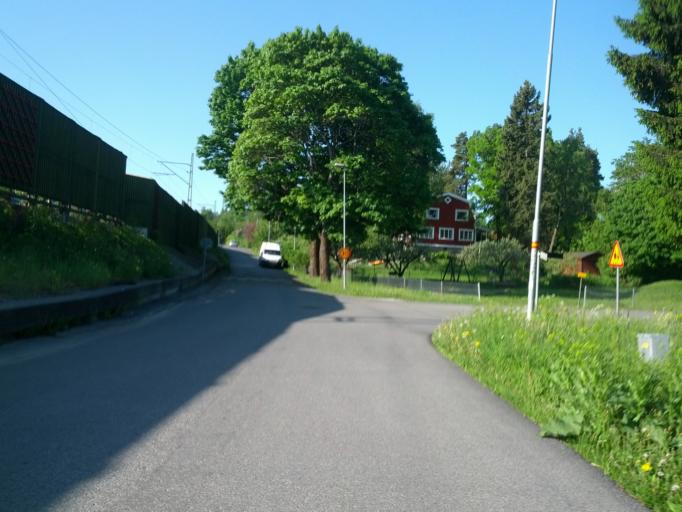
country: SE
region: Stockholm
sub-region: Taby Kommun
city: Taby
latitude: 59.4324
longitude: 18.0525
